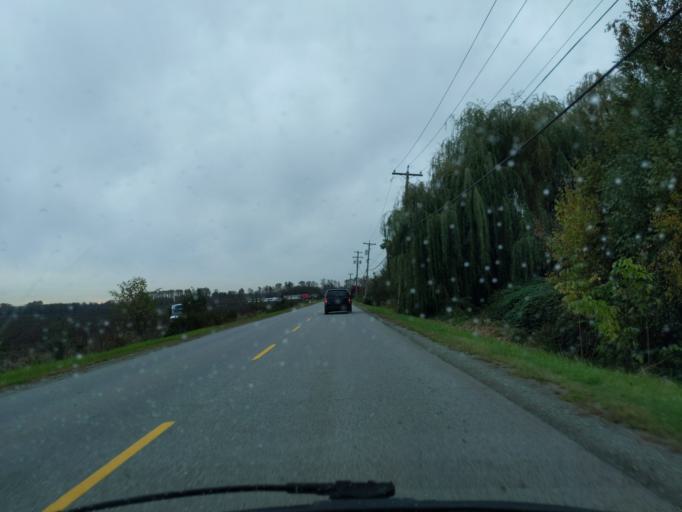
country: CA
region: British Columbia
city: Pitt Meadows
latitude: 49.2201
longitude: -122.7228
